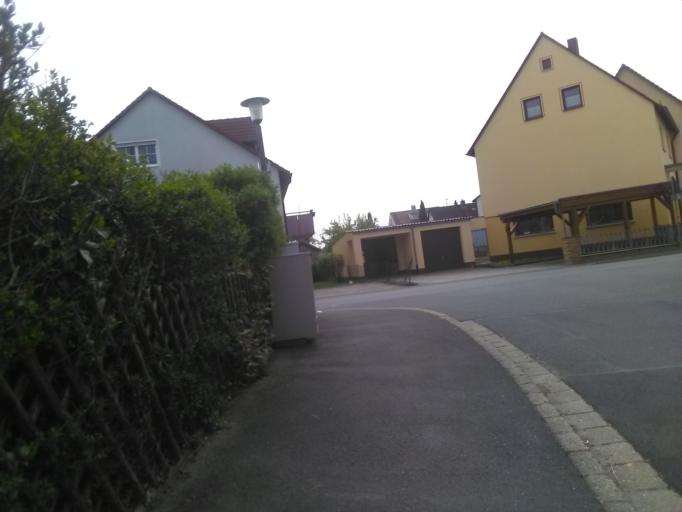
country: DE
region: Bavaria
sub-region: Upper Franconia
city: Kleinsendelbach
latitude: 49.5711
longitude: 11.2010
